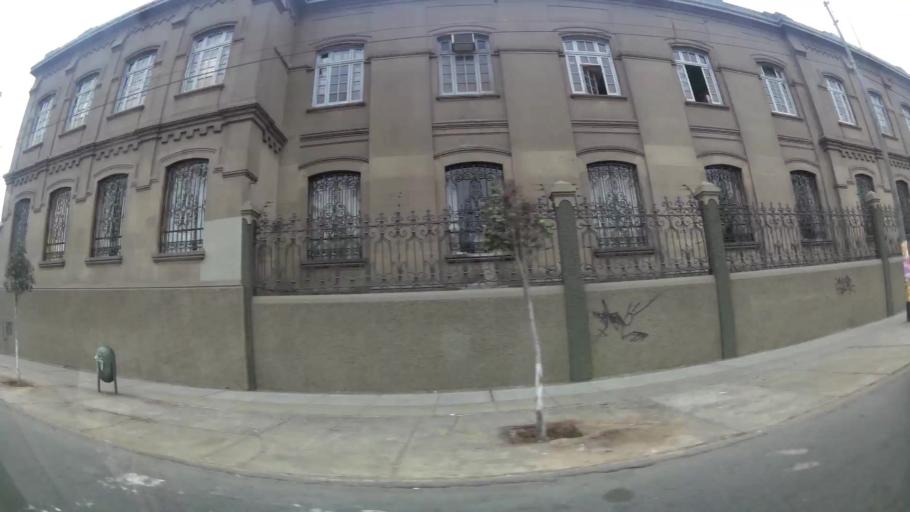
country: PE
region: Lima
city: Lima
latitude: -12.0618
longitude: -77.0430
